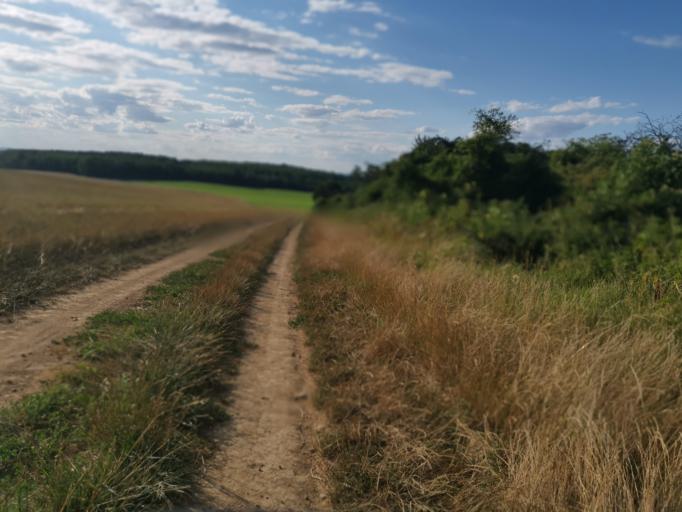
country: CZ
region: South Moravian
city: Sudomerice
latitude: 48.8166
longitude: 17.2795
